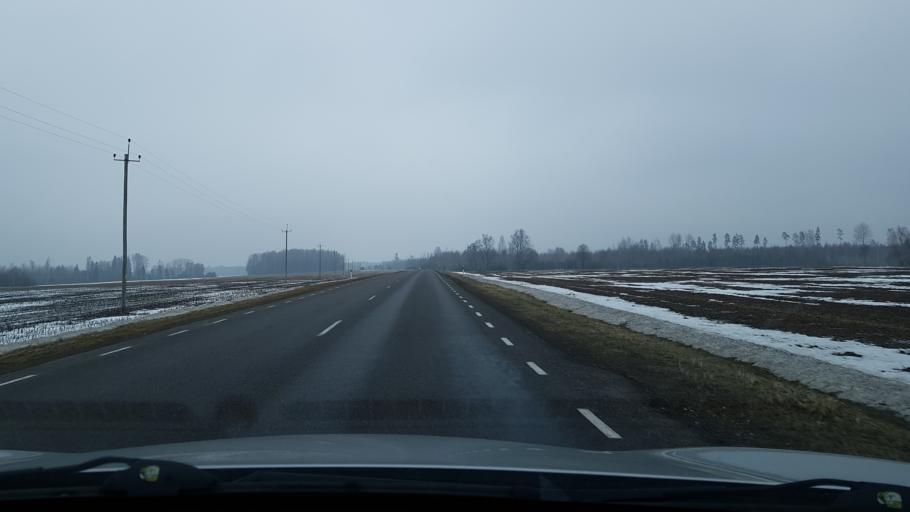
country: EE
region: Valgamaa
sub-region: Torva linn
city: Torva
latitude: 58.0950
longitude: 26.0107
